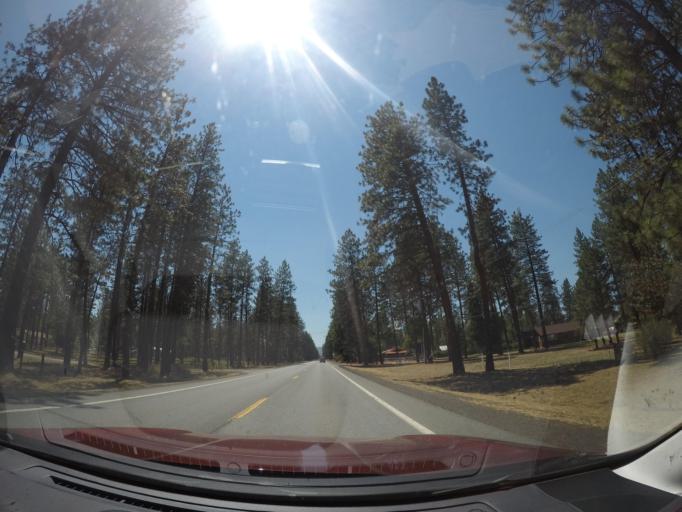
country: US
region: California
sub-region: Shasta County
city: Burney
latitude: 41.0637
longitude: -121.3606
